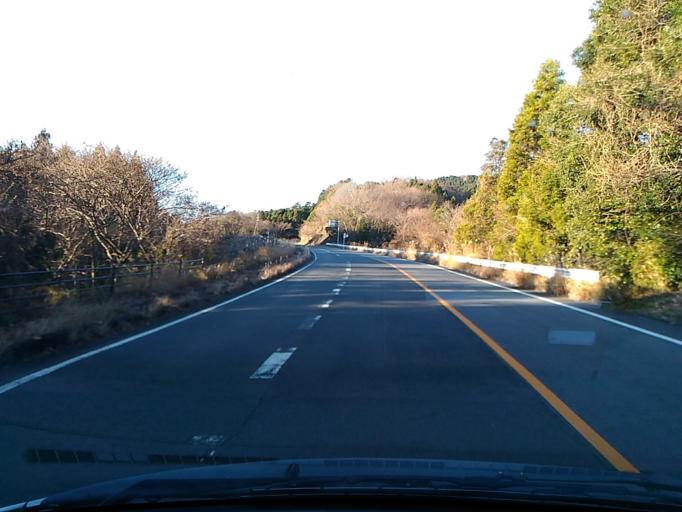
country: JP
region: Ibaraki
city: Kitaibaraki
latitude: 36.9074
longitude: 140.7267
